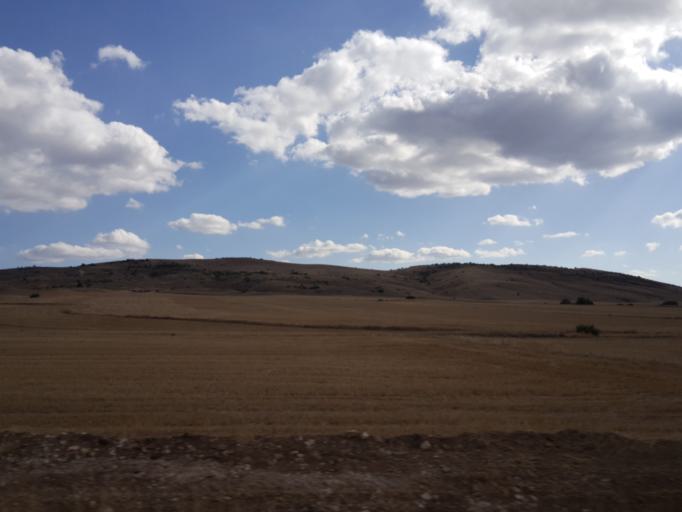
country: TR
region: Tokat
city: Sulusaray
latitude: 39.9865
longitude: 35.9586
